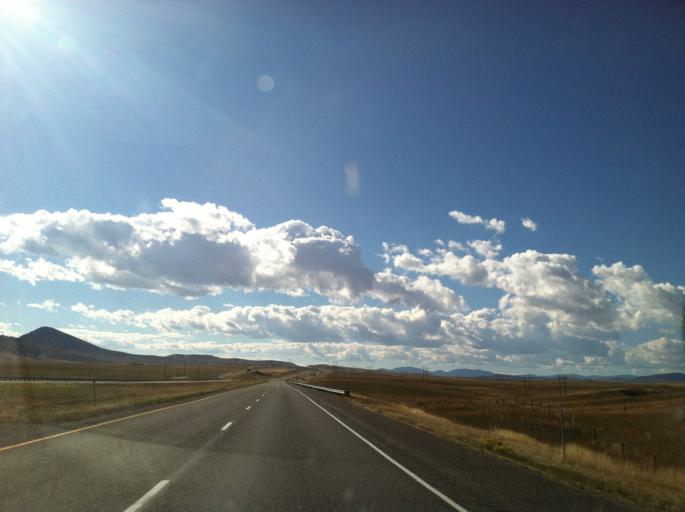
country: US
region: Montana
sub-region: Gallatin County
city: Three Forks
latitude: 45.9185
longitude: -111.6072
